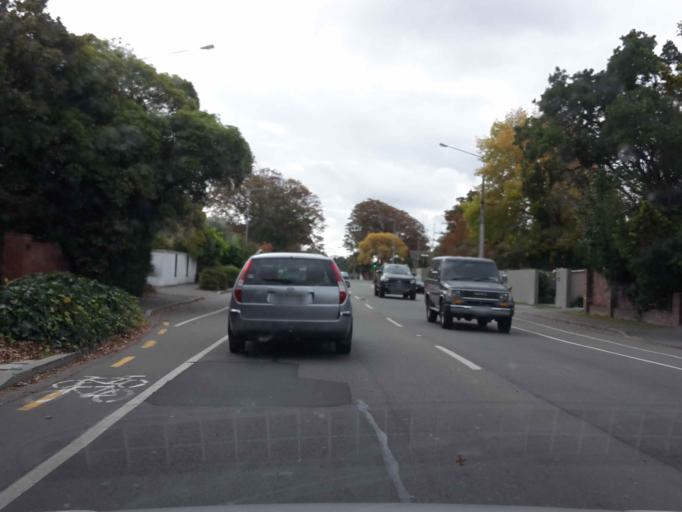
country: NZ
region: Canterbury
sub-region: Christchurch City
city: Christchurch
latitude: -43.5210
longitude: 172.6011
